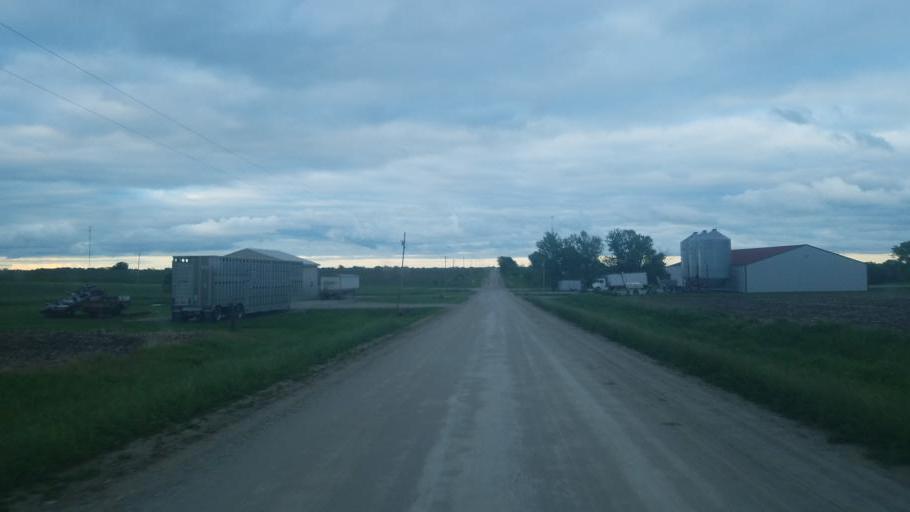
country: US
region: Iowa
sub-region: Decatur County
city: Lamoni
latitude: 40.5947
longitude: -93.9413
